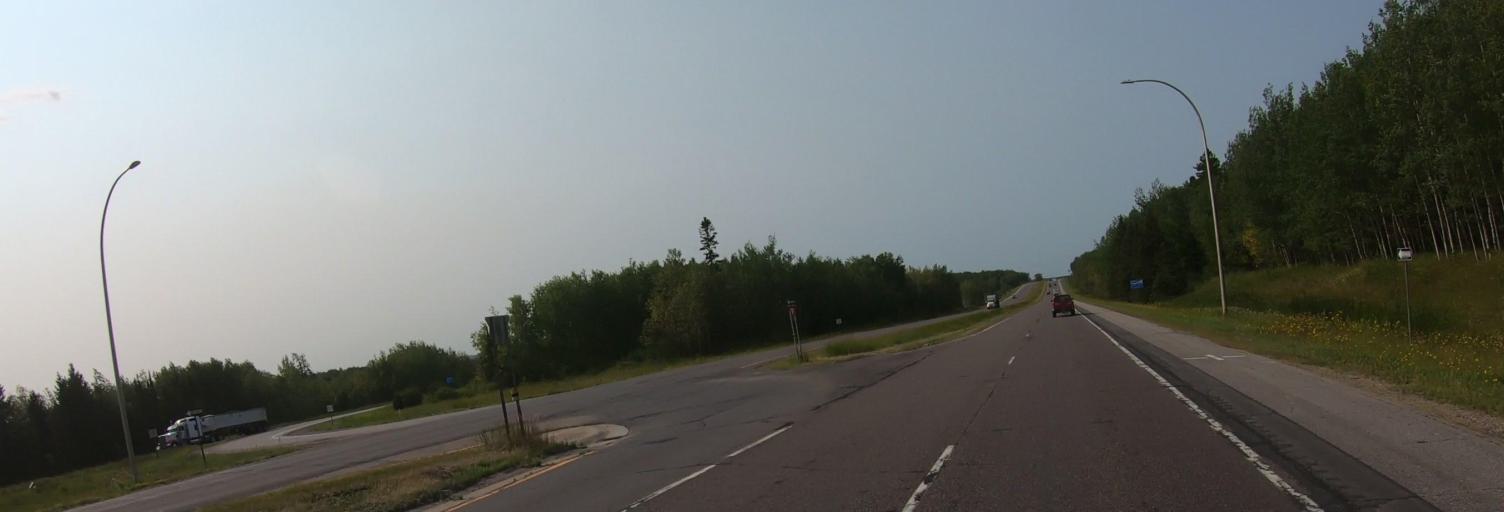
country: US
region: Minnesota
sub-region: Saint Louis County
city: Virginia
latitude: 47.5563
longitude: -92.5474
